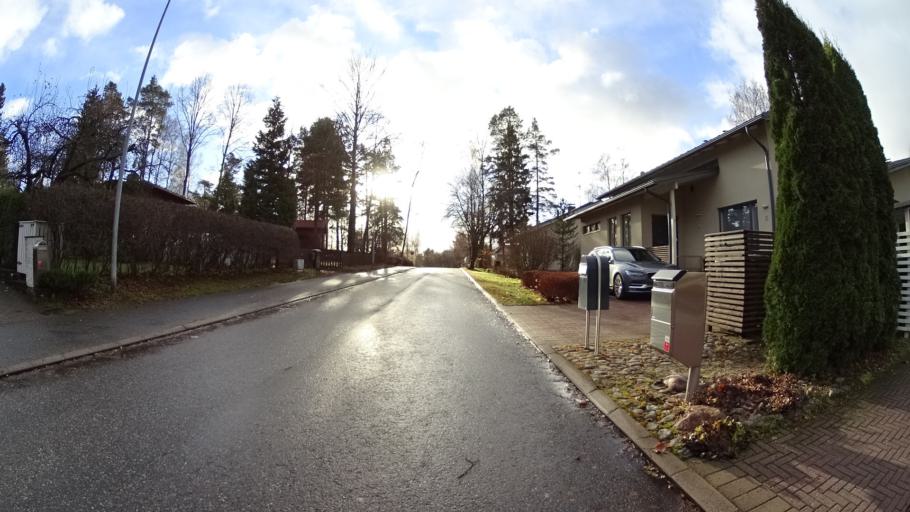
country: FI
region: Uusimaa
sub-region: Helsinki
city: Kilo
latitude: 60.1864
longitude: 24.7811
